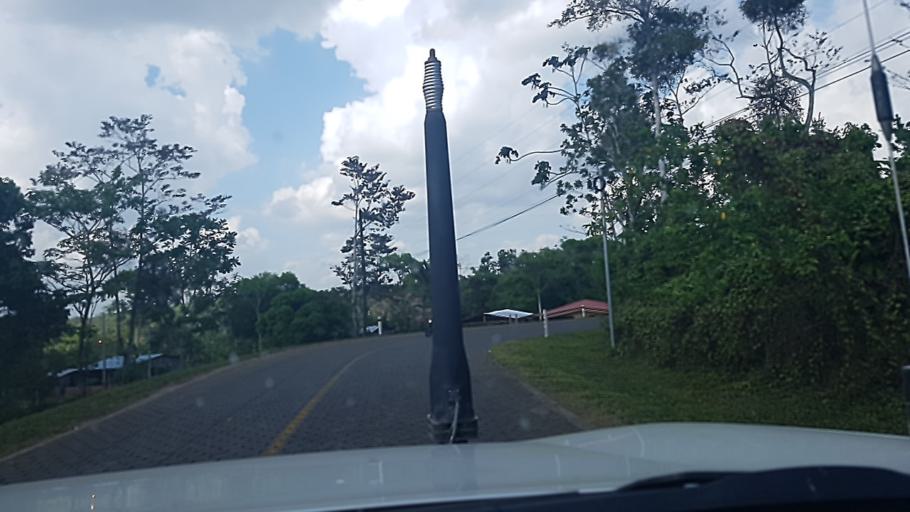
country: NI
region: Atlantico Sur
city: Nueva Guinea
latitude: 11.7043
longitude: -84.3753
